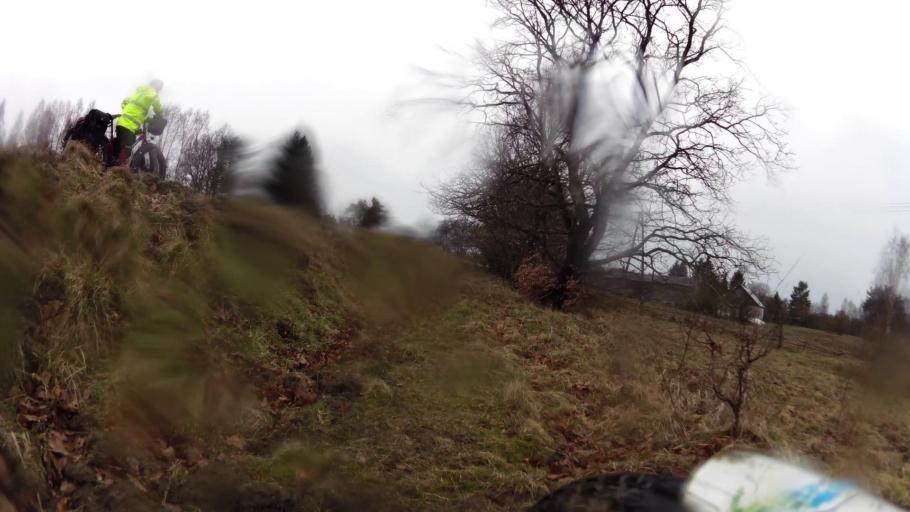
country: PL
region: Pomeranian Voivodeship
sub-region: Powiat bytowski
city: Miastko
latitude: 54.0397
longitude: 17.0367
